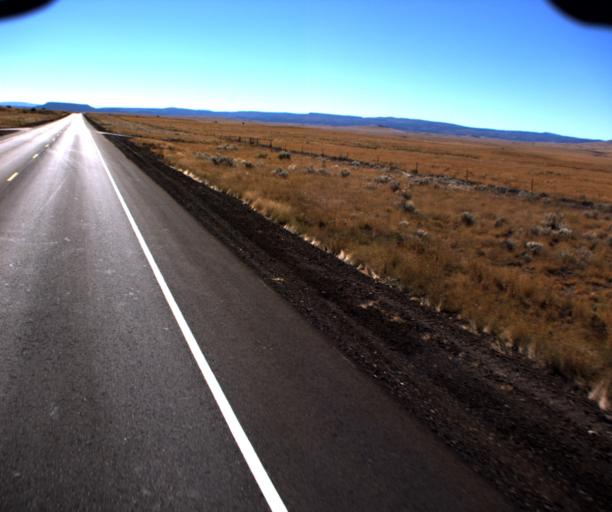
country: US
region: Arizona
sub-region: Apache County
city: Springerville
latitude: 34.2307
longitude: -109.3409
